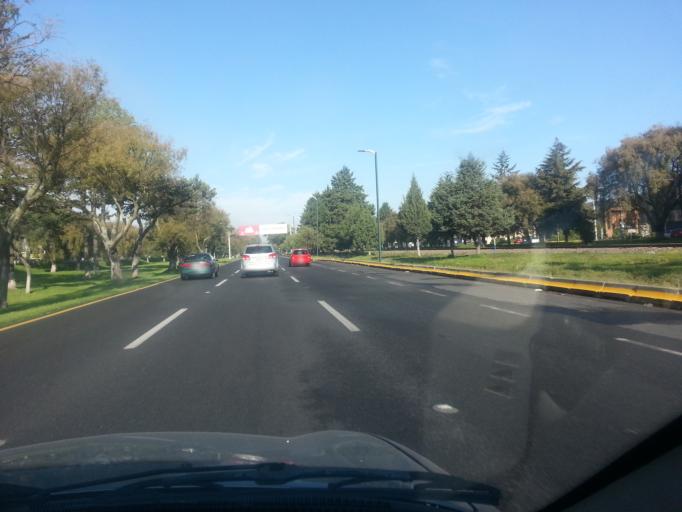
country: MX
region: Mexico
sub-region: San Mateo Atenco
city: Santa Maria la Asuncion
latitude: 19.2865
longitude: -99.5604
